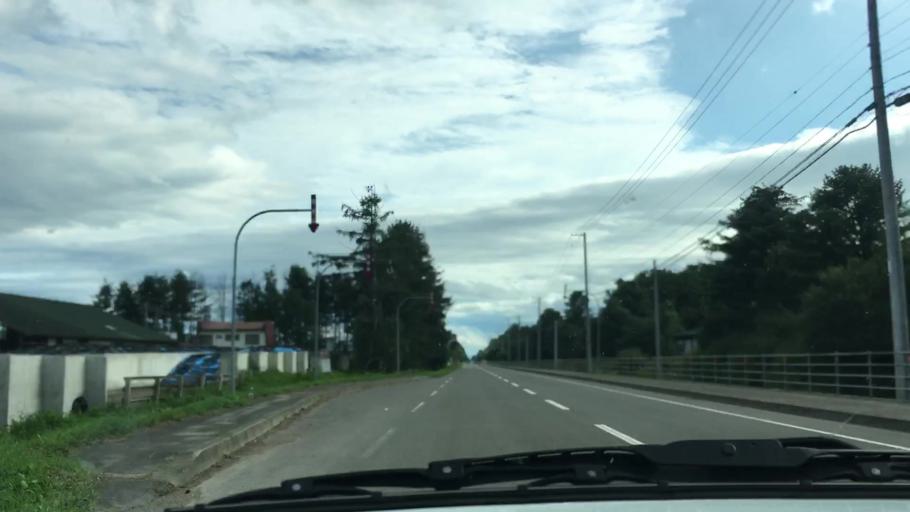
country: JP
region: Hokkaido
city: Otofuke
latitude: 43.2494
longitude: 143.2989
